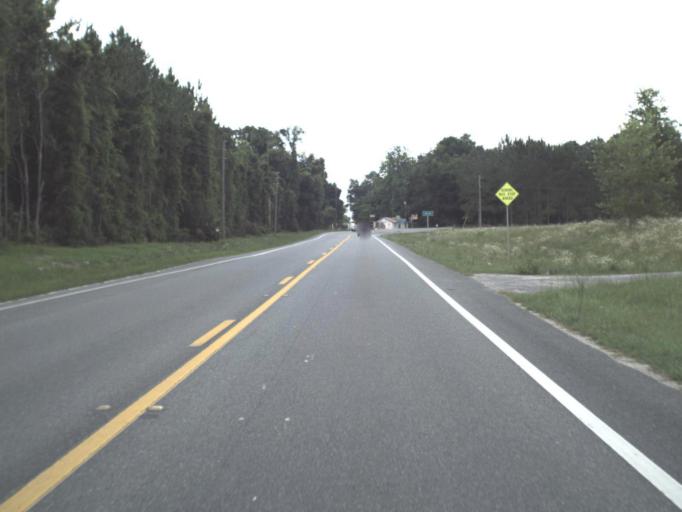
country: US
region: Florida
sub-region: Levy County
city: Manatee Road
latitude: 29.6070
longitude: -82.9234
